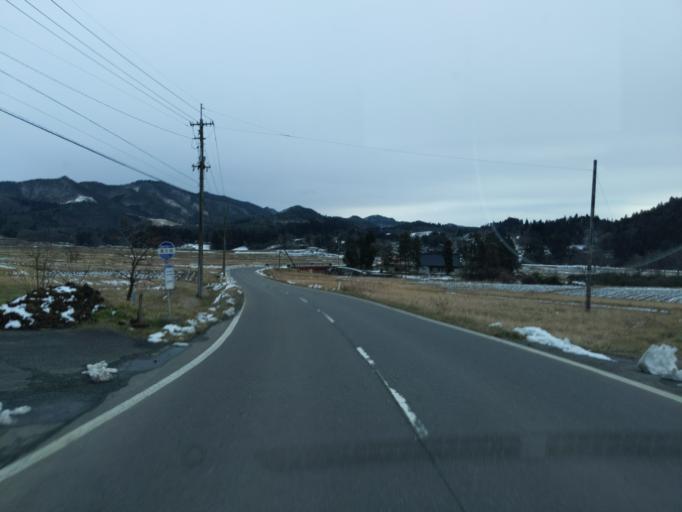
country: JP
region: Iwate
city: Mizusawa
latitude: 39.1779
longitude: 141.2497
